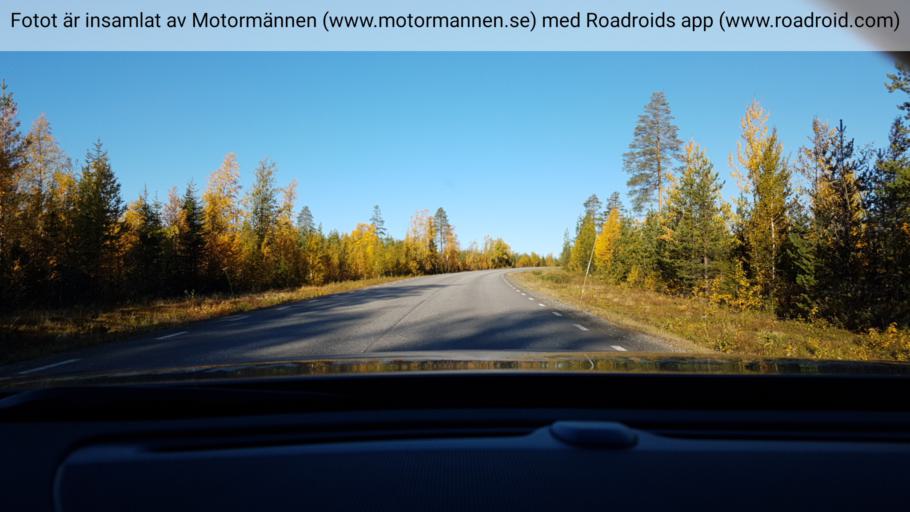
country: SE
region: Vaesterbotten
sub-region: Skelleftea Kommun
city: Storvik
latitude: 65.3386
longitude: 20.5282
